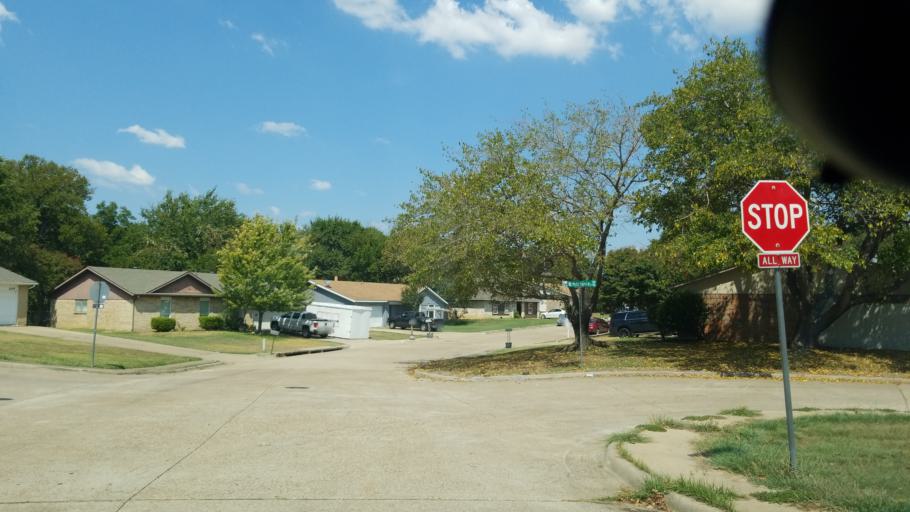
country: US
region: Texas
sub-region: Dallas County
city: Grand Prairie
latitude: 32.7161
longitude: -96.9917
